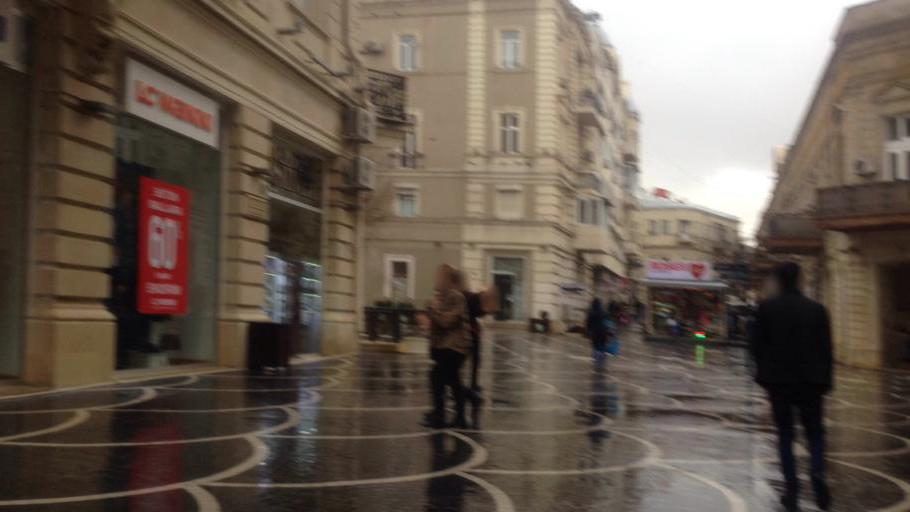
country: AZ
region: Baki
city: Badamdar
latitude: 40.3723
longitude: 49.8390
